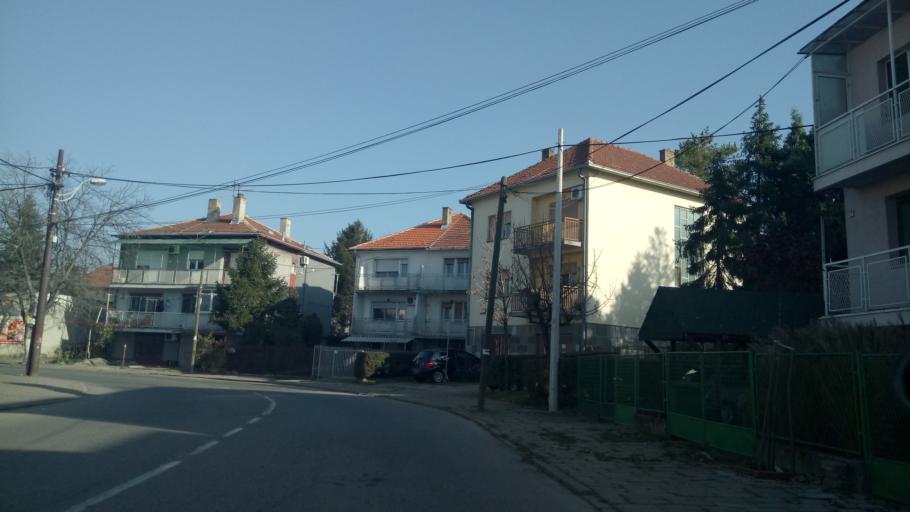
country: RS
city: Novi Banovci
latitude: 44.9006
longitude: 20.2950
